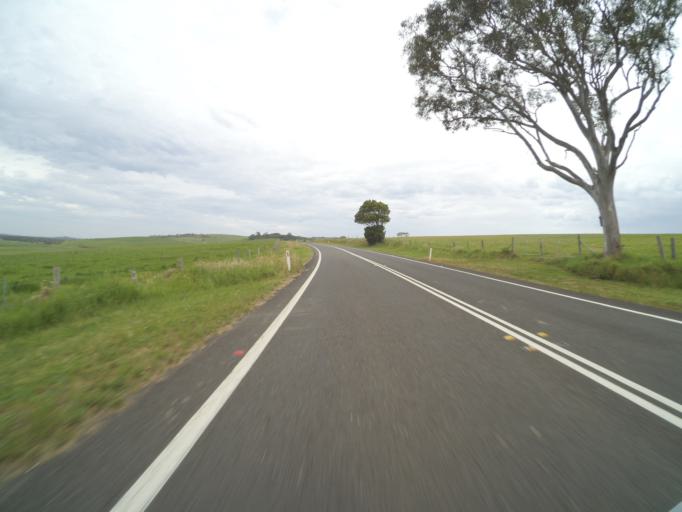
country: AU
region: New South Wales
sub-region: Kiama
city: Jamberoo
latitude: -34.6536
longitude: 150.8142
